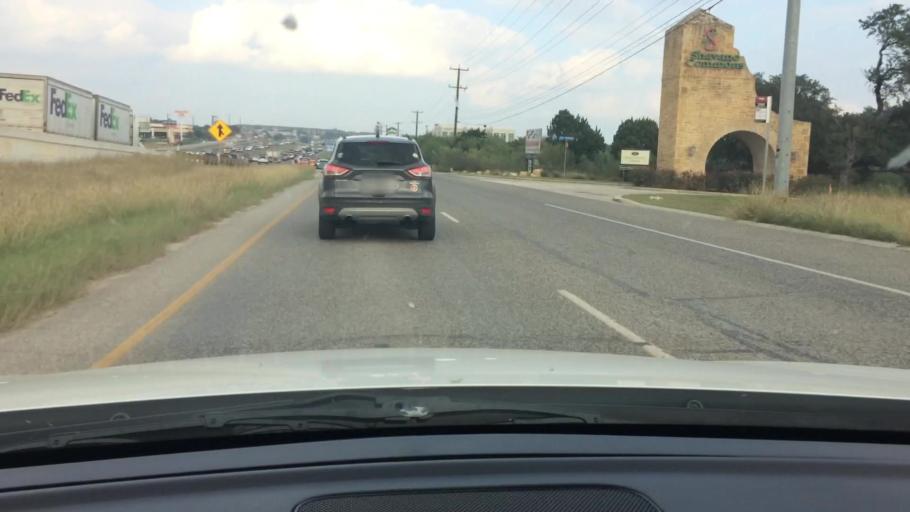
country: US
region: Texas
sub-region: Bexar County
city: Shavano Park
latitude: 29.5952
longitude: -98.5765
